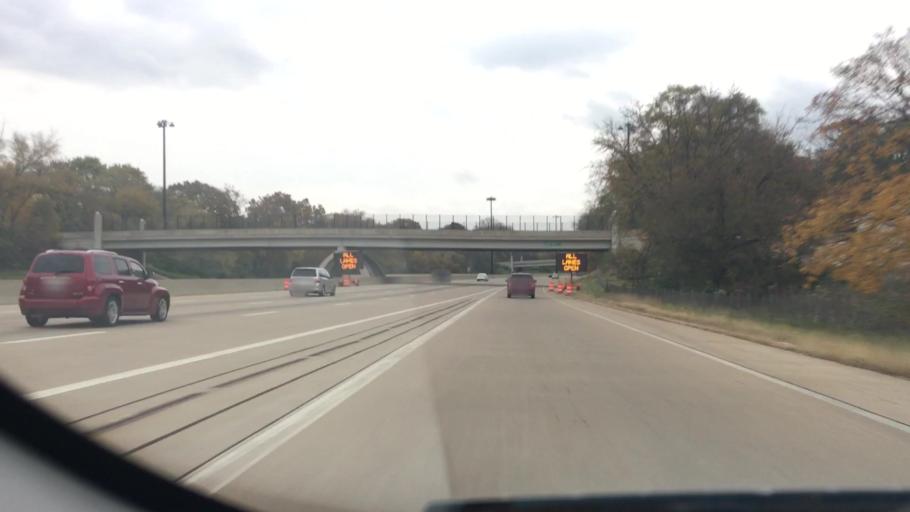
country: US
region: Illinois
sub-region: Peoria County
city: Peoria
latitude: 40.7068
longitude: -89.6086
